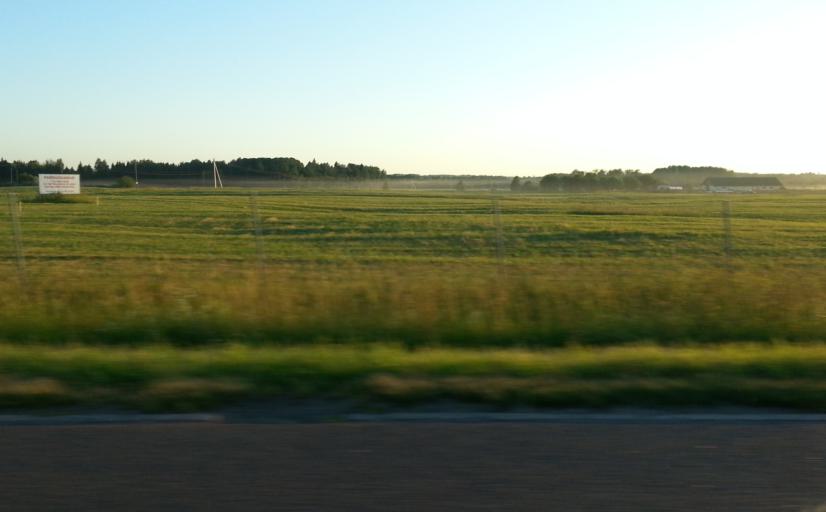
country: LT
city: Sirvintos
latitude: 55.1204
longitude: 24.8428
